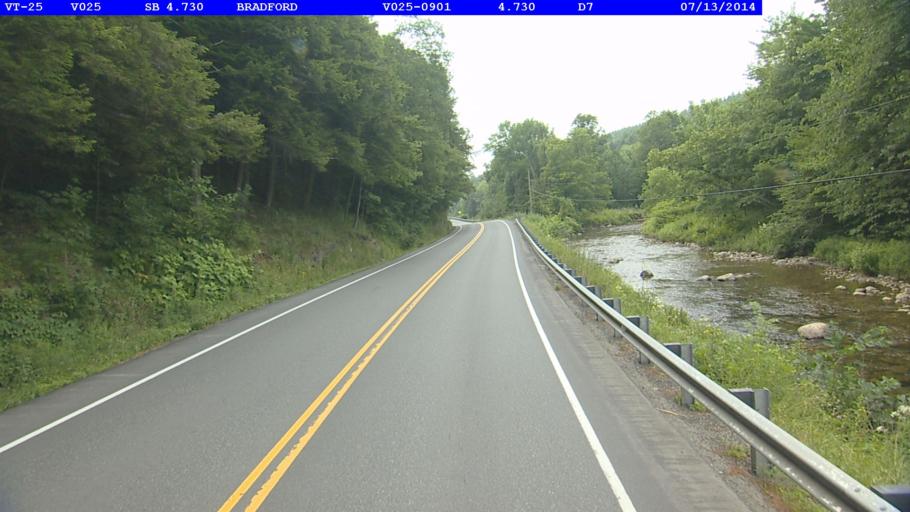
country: US
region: New Hampshire
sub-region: Grafton County
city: Haverhill
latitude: 44.0207
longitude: -72.1735
